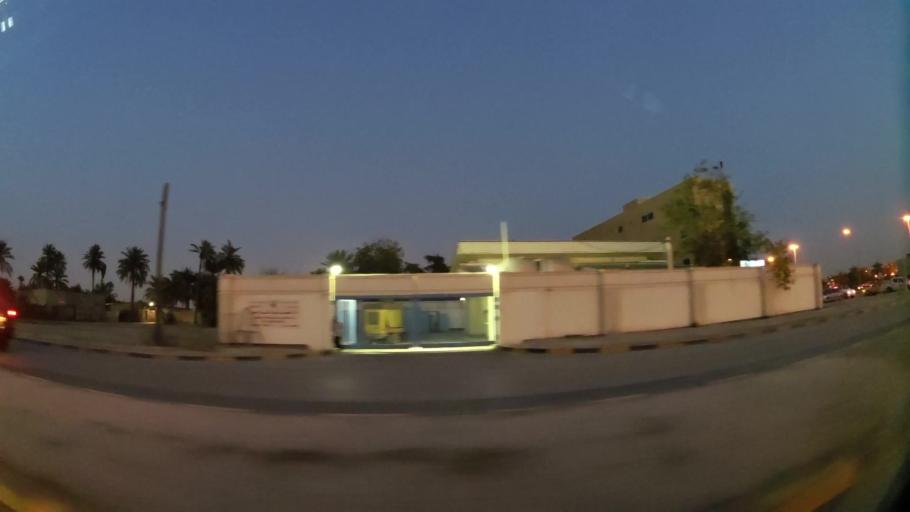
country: BH
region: Manama
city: Jidd Hafs
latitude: 26.1991
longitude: 50.5529
